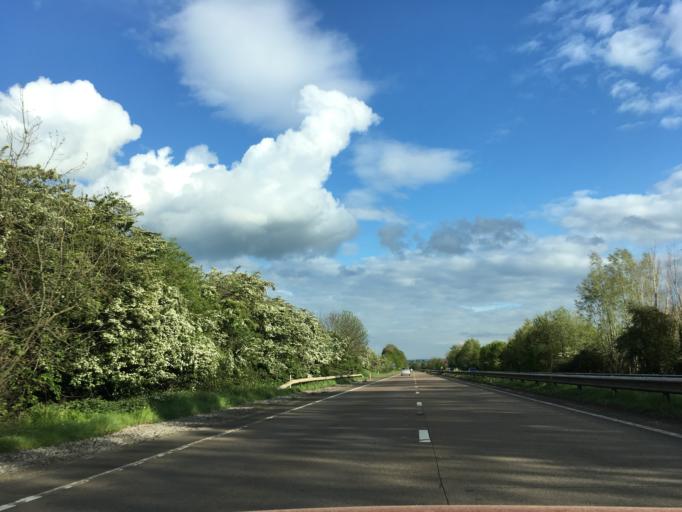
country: GB
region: Wales
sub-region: Monmouthshire
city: Abergavenny
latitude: 51.7973
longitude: -2.9978
